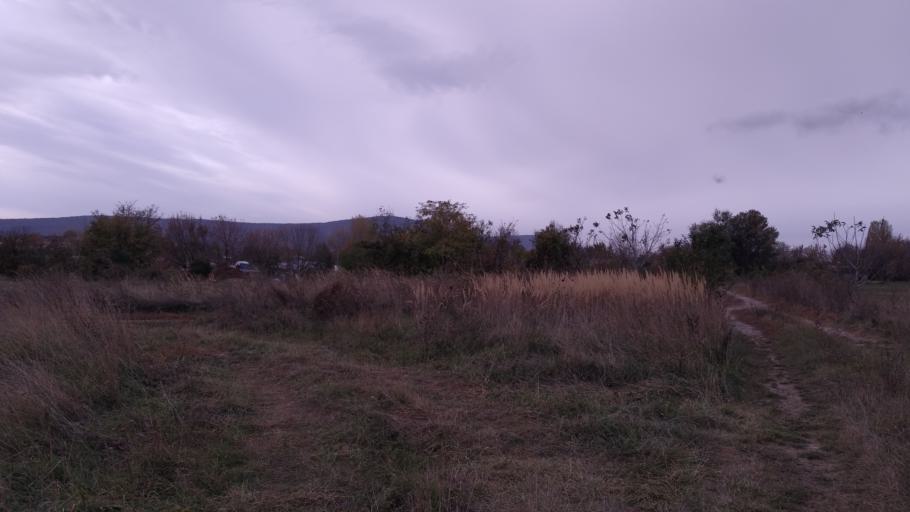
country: HU
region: Pest
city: Pomaz
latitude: 47.6384
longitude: 19.0465
